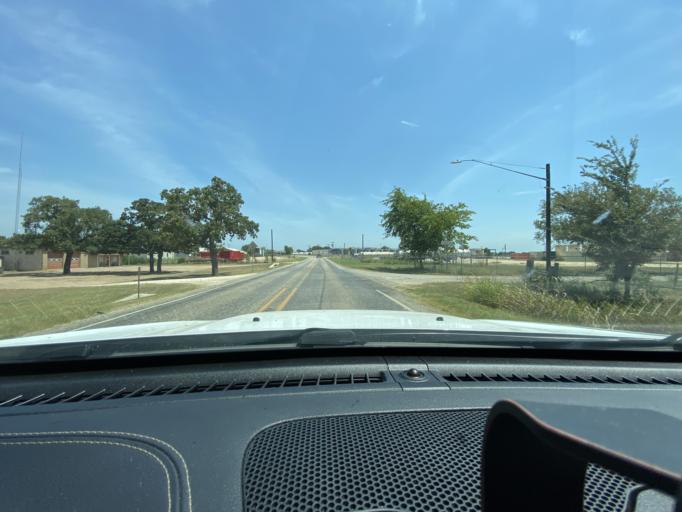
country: US
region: Texas
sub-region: Lee County
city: Giddings
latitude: 30.1662
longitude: -96.9428
